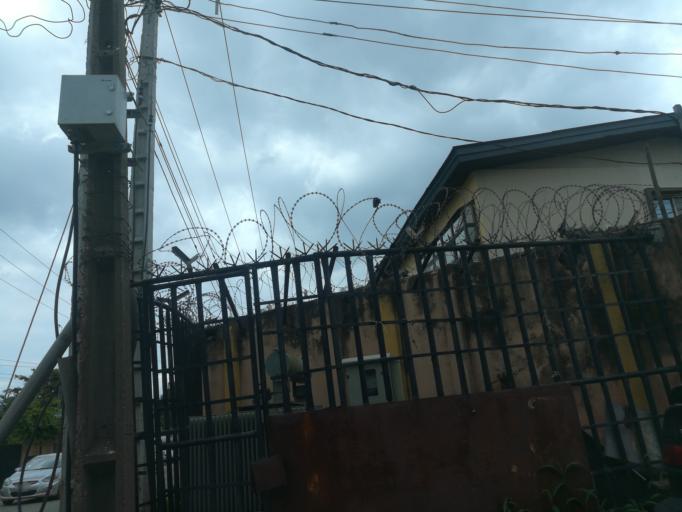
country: NG
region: Lagos
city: Somolu
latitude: 6.5546
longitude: 3.3622
